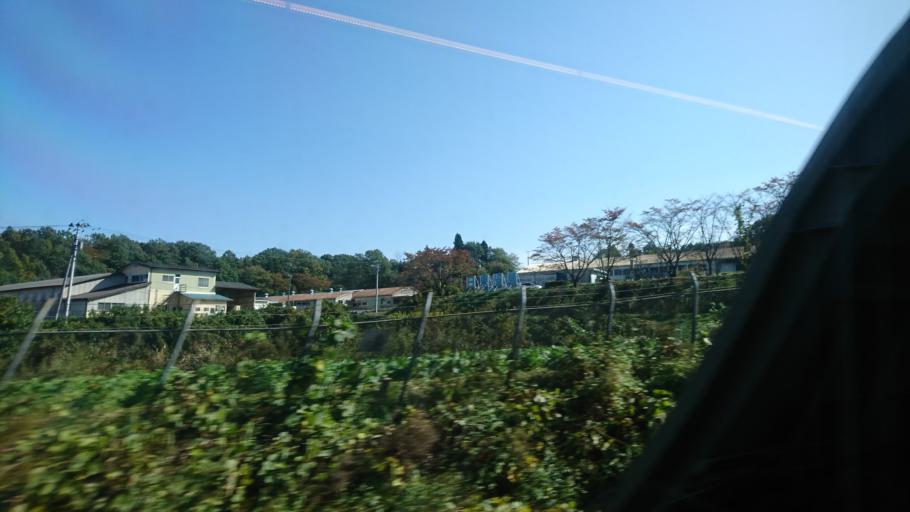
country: JP
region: Fukushima
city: Nihommatsu
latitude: 37.5923
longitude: 140.4698
